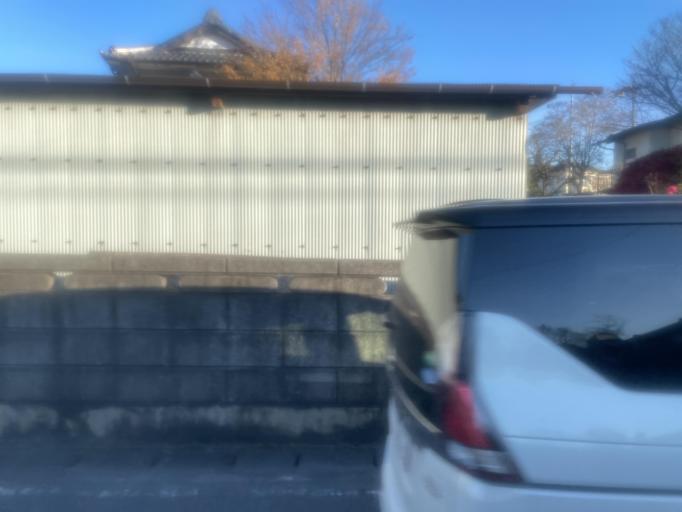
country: JP
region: Saitama
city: Yorii
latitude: 36.1099
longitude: 139.1999
